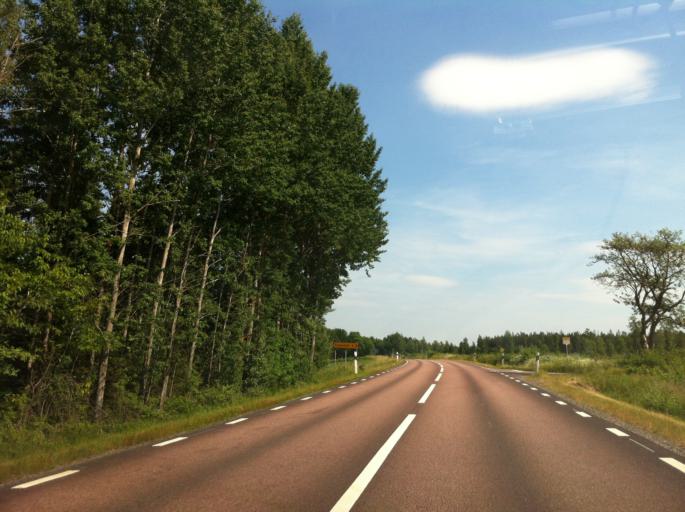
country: SE
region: Kalmar
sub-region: Nybro Kommun
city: Nybro
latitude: 56.7850
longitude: 15.8076
